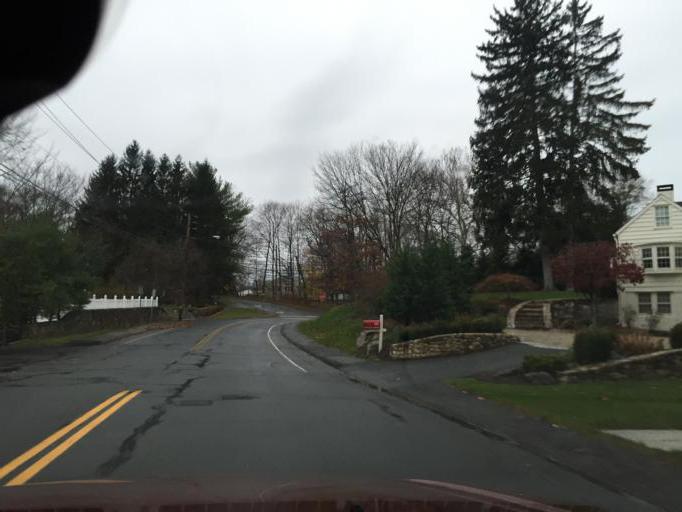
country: US
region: Connecticut
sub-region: Fairfield County
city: East Norwalk
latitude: 41.1233
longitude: -73.3805
